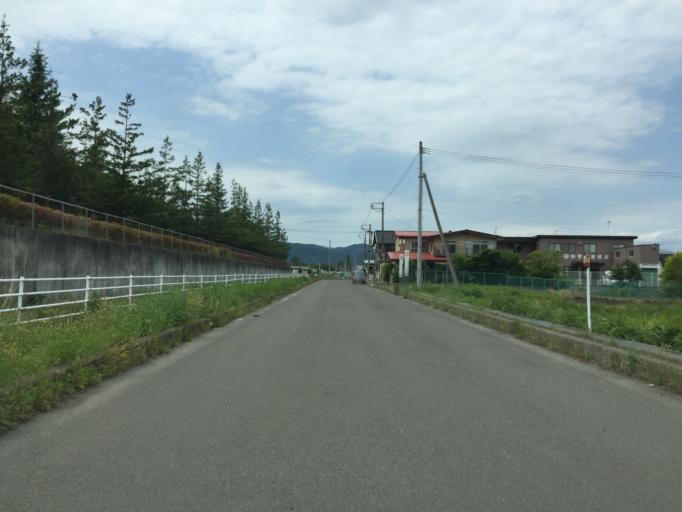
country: JP
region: Fukushima
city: Fukushima-shi
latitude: 37.7376
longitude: 140.4024
